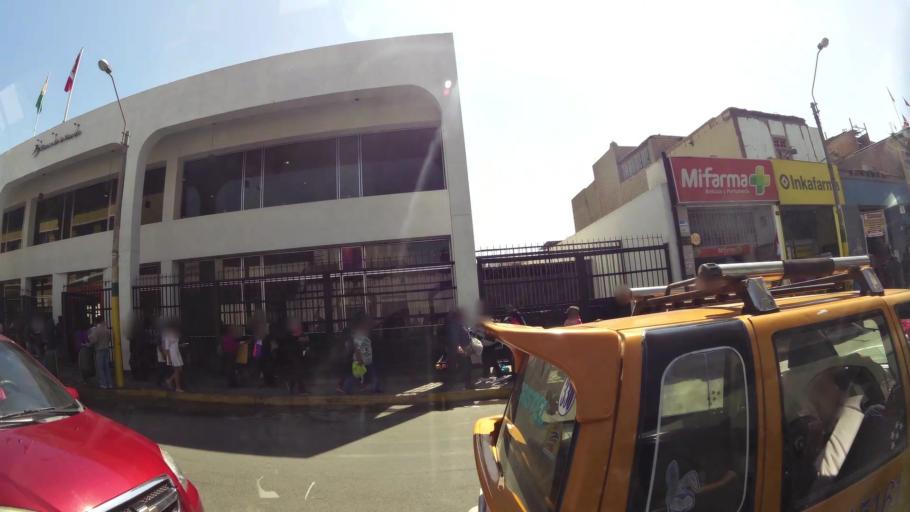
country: PE
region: Ica
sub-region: Provincia de Ica
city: Ica
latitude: -14.0632
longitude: -75.7281
